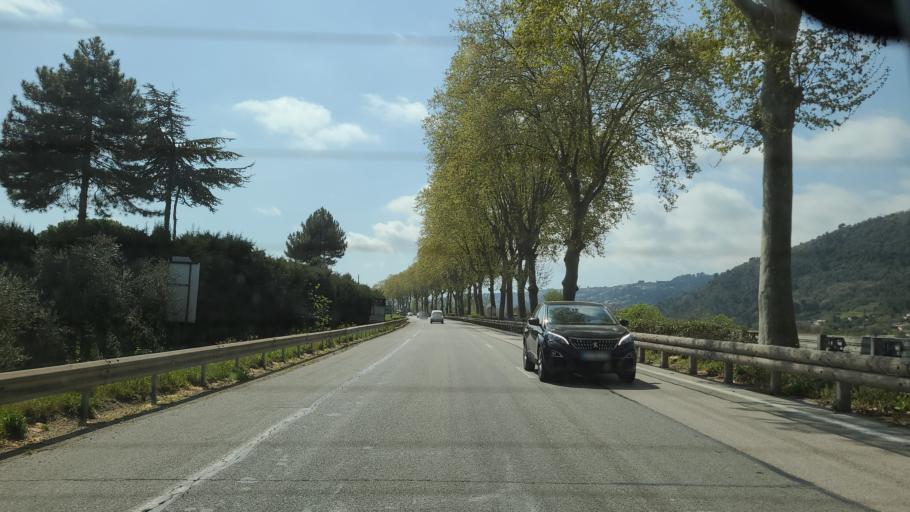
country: FR
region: Provence-Alpes-Cote d'Azur
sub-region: Departement des Alpes-Maritimes
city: Gattieres
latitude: 43.7393
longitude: 7.1843
